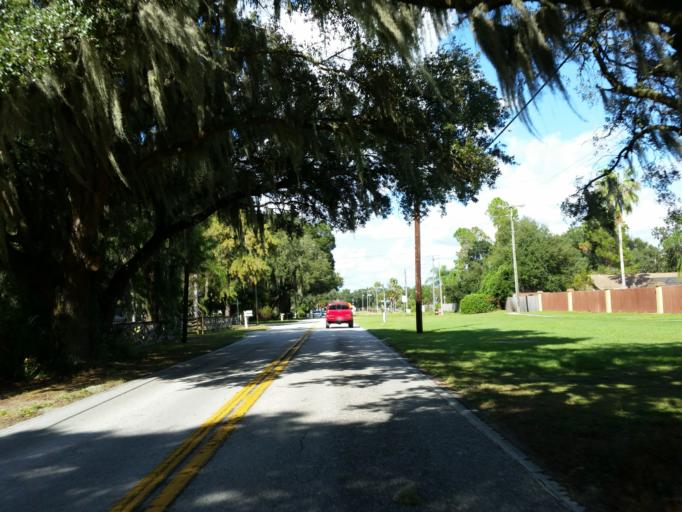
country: US
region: Florida
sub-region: Hillsborough County
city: Brandon
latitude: 27.9039
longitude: -82.2775
